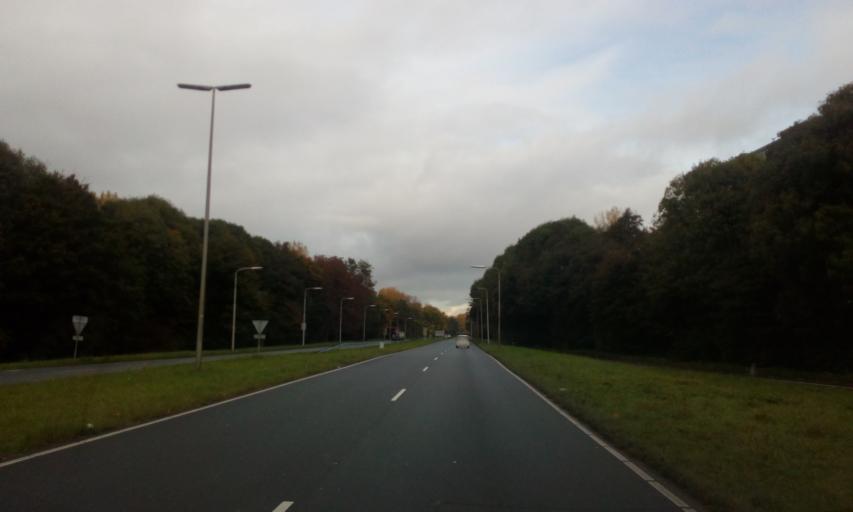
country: NL
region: South Holland
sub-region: Gemeente Delft
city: Delft
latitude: 51.9883
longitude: 4.3518
